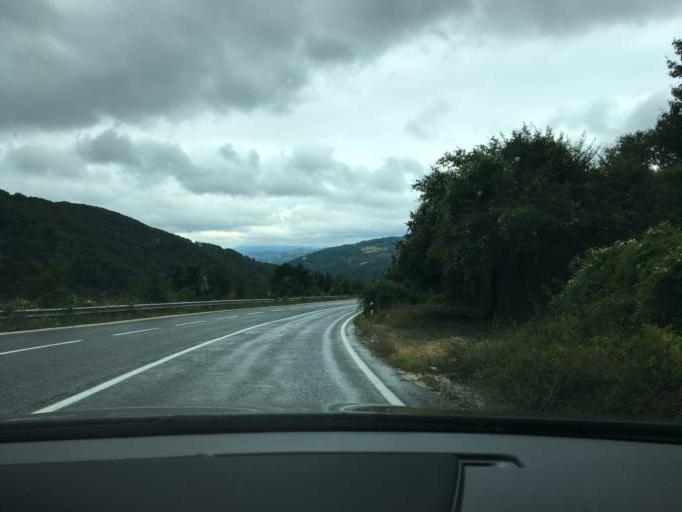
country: MK
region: Kriva Palanka
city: Kriva Palanka
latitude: 42.2180
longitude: 22.4371
